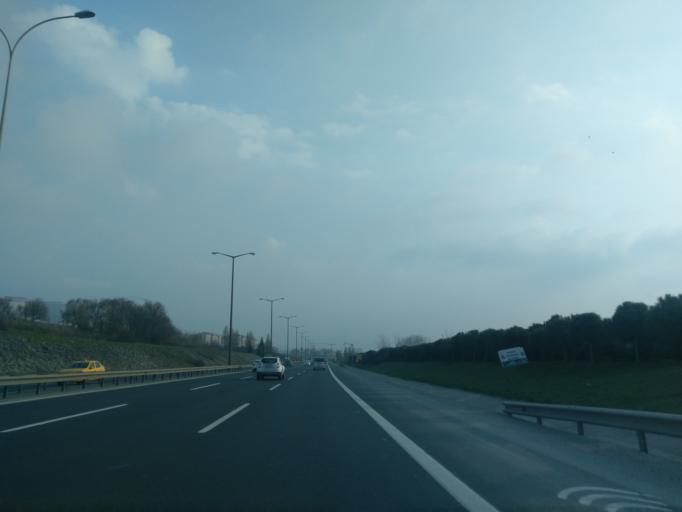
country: TR
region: Istanbul
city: Esenyurt
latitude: 41.0706
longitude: 28.6495
